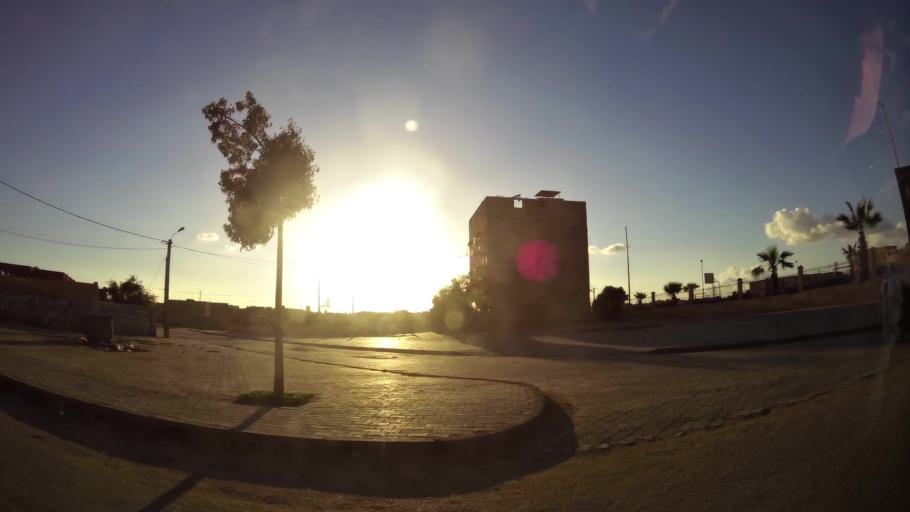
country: MA
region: Marrakech-Tensift-Al Haouz
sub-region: Kelaa-Des-Sraghna
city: Sidi Abdallah
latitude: 32.2471
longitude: -7.9469
